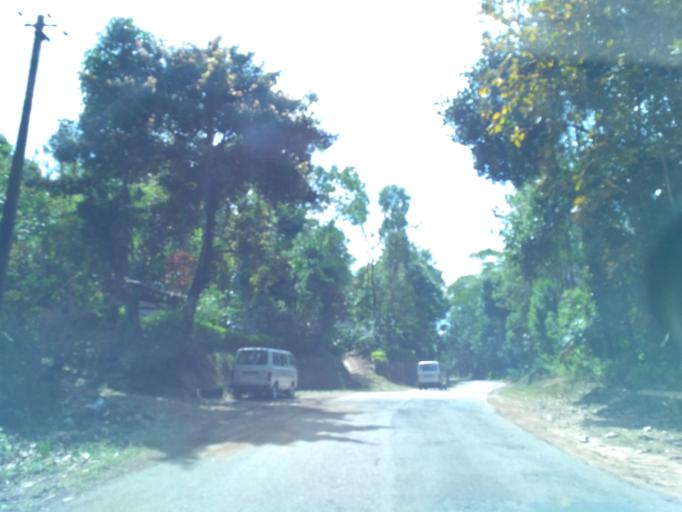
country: IN
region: Karnataka
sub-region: Kodagu
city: Madikeri
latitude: 12.3850
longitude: 75.7103
